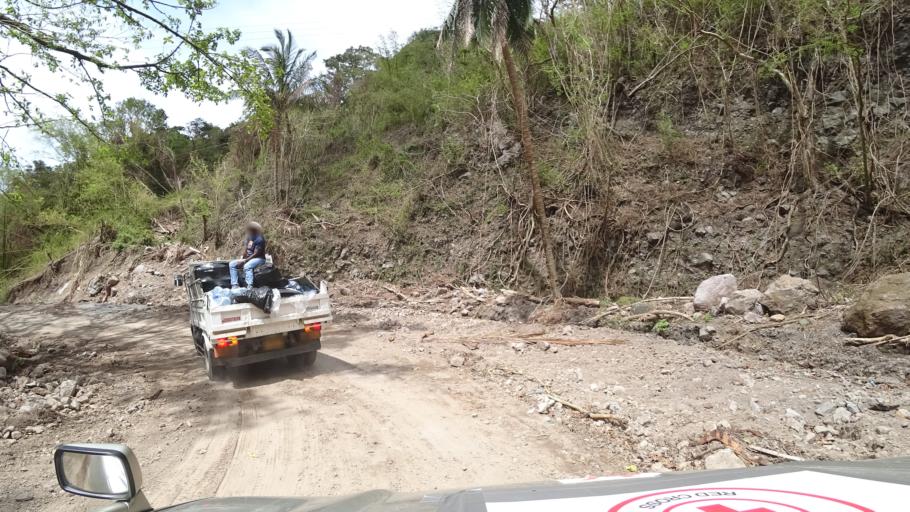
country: DM
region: Saint Mark
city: Soufriere
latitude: 15.2380
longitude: -61.3643
